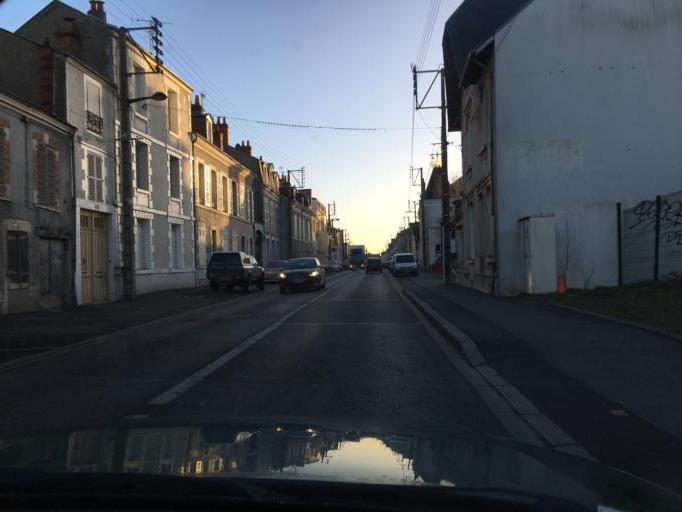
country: FR
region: Centre
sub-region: Departement du Loiret
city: Saint-Jean-le-Blanc
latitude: 47.9020
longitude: 1.9250
